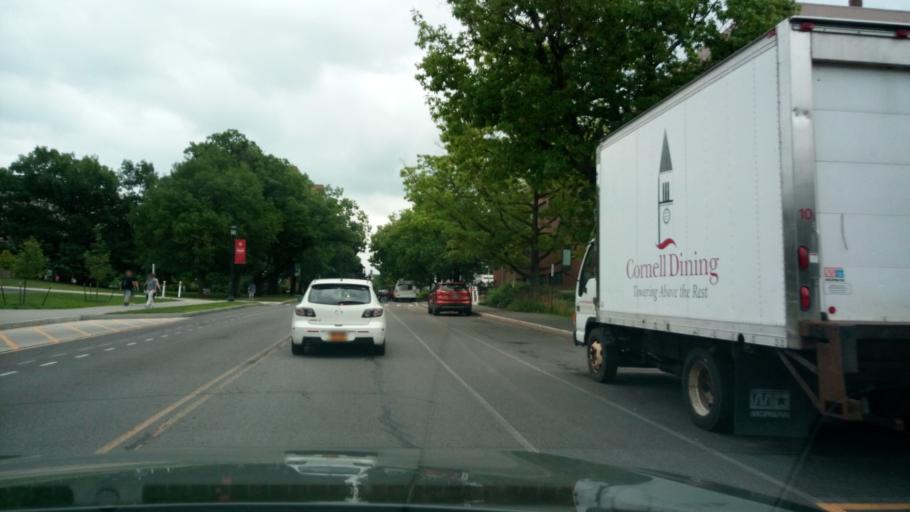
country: US
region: New York
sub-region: Tompkins County
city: East Ithaca
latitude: 42.4476
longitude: -76.4793
